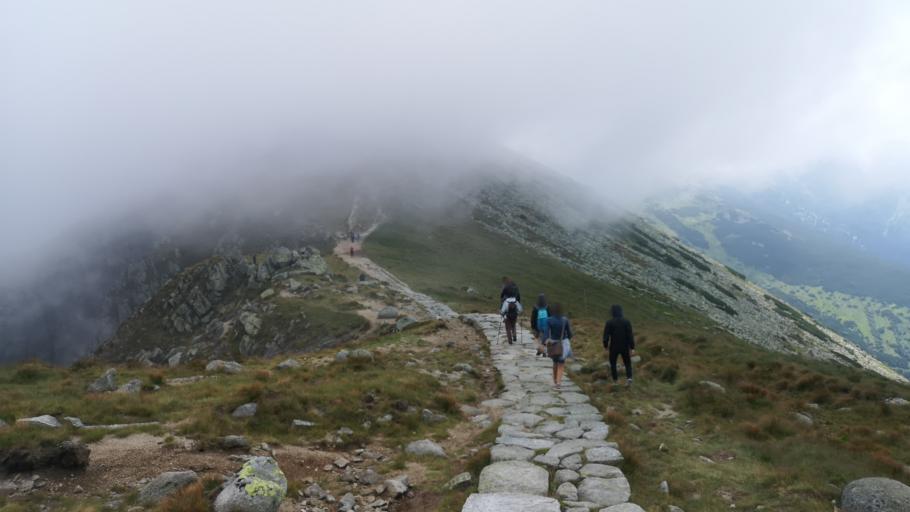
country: SK
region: Banskobystricky
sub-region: Okres Banska Bystrica
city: Brezno
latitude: 48.9408
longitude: 19.6006
